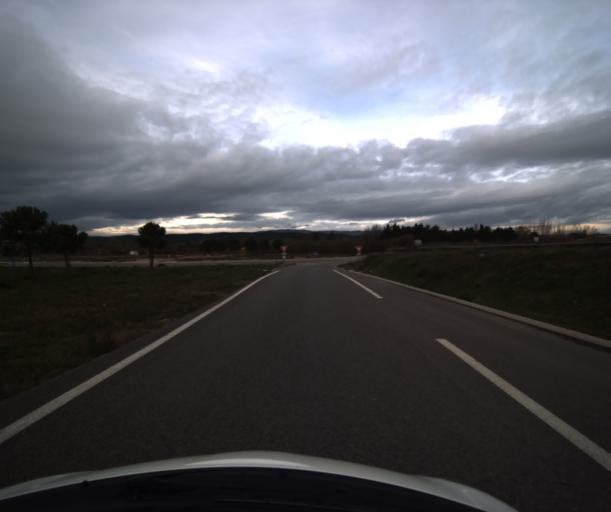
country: FR
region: Provence-Alpes-Cote d'Azur
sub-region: Departement du Vaucluse
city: Pertuis
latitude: 43.6872
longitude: 5.4836
